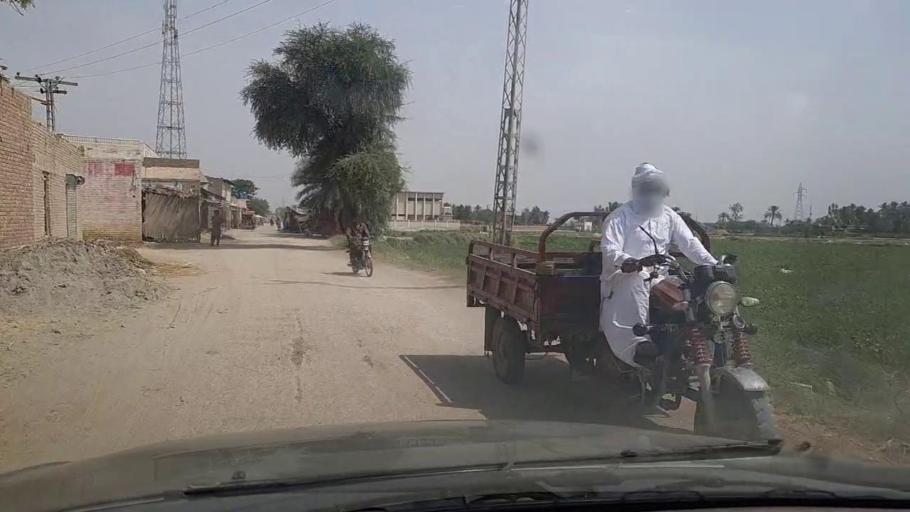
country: PK
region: Sindh
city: Shikarpur
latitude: 27.9296
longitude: 68.6613
